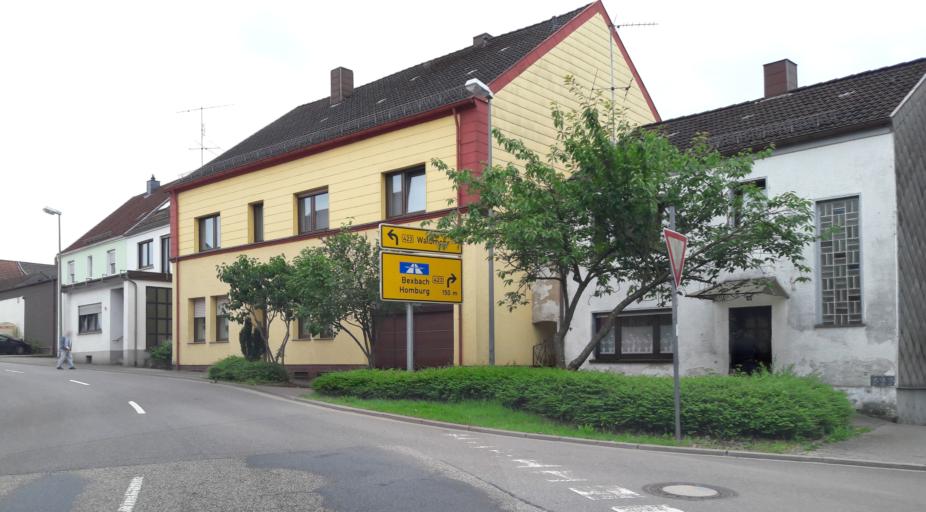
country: DE
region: Rheinland-Pfalz
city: Waldmohr
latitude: 49.3704
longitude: 7.3222
